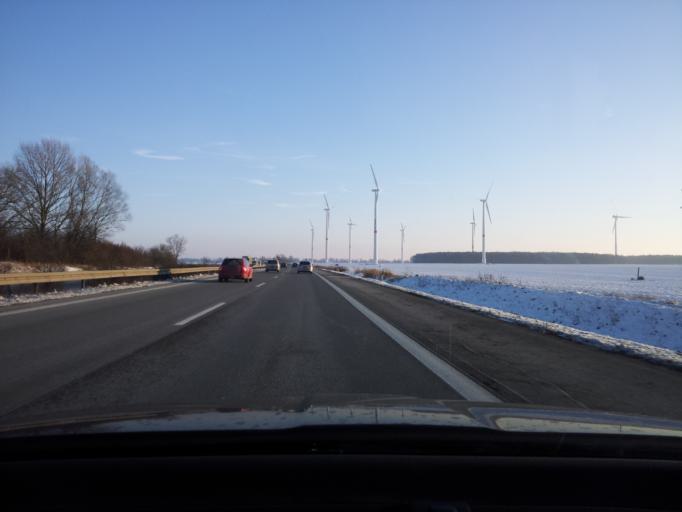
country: DE
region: Brandenburg
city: Heiligengrabe
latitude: 53.1918
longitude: 12.2815
